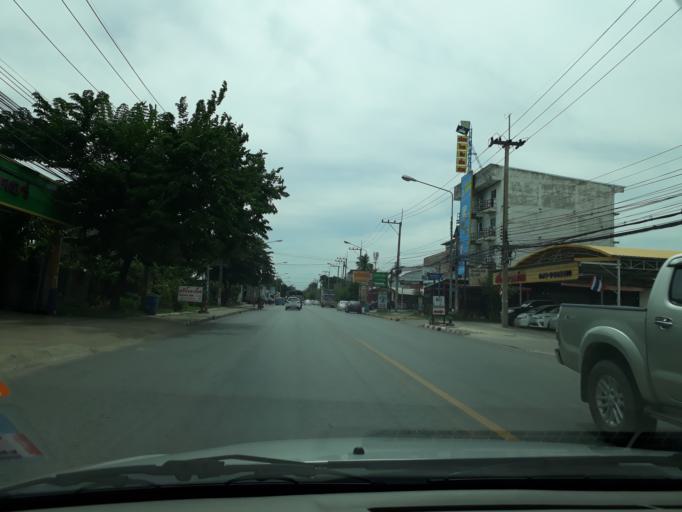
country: TH
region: Khon Kaen
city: Khon Kaen
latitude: 16.4363
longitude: 102.8495
